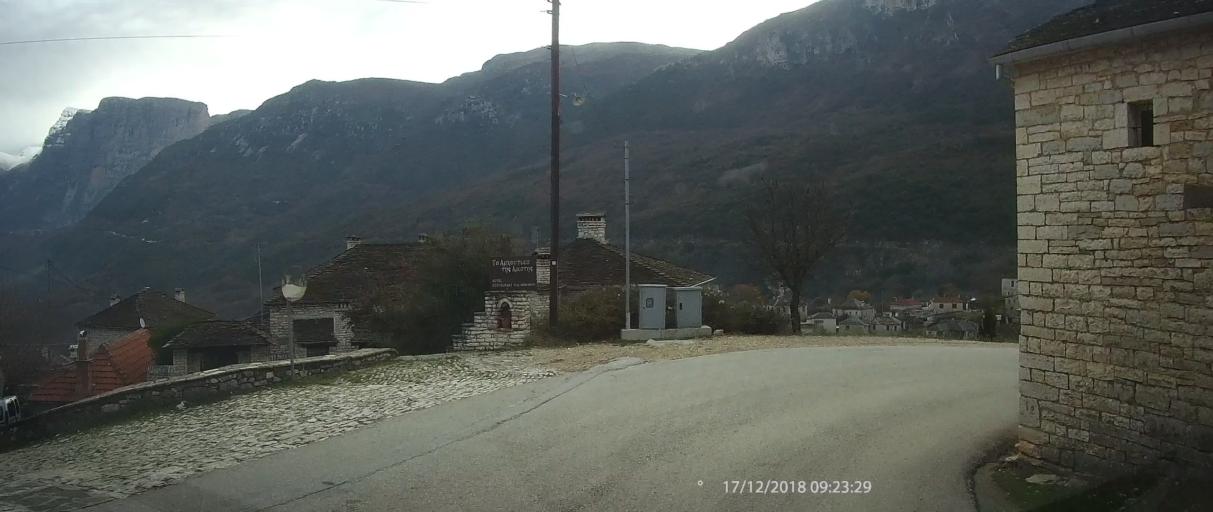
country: GR
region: Epirus
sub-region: Nomos Ioanninon
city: Kalpaki
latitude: 39.9356
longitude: 20.6714
